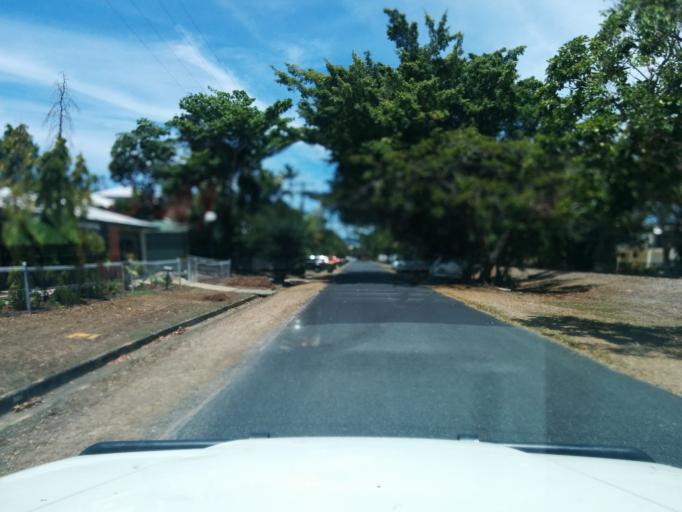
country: AU
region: Queensland
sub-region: Cairns
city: Cairns
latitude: -16.9116
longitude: 145.7603
